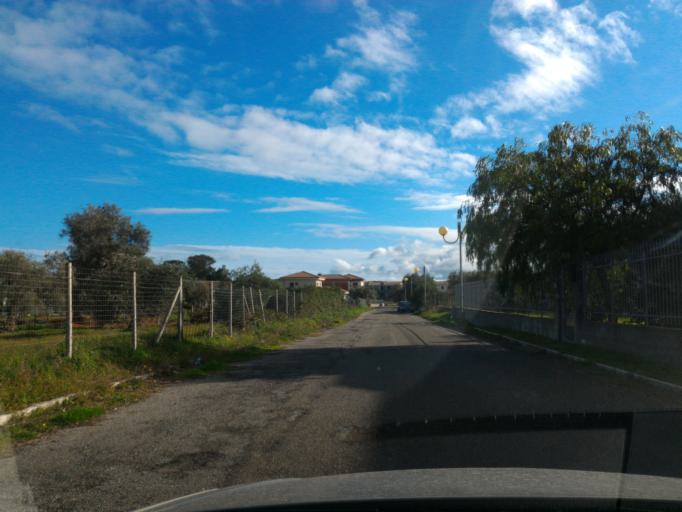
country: IT
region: Calabria
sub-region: Provincia di Crotone
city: Torretta
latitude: 39.4587
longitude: 17.0332
